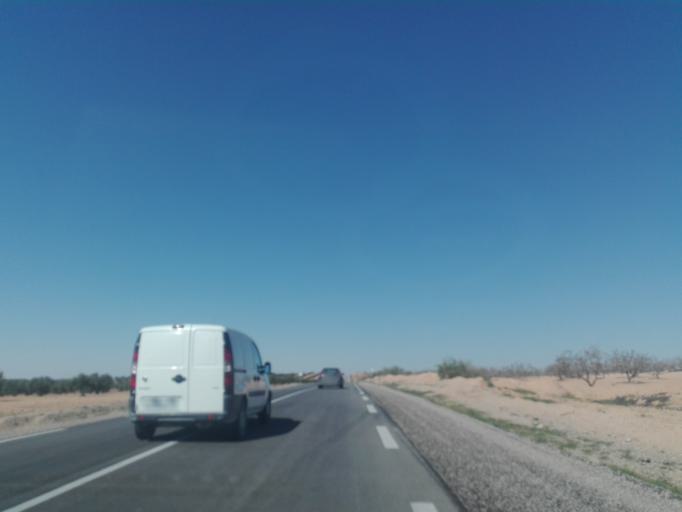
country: TN
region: Safaqis
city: Bi'r `Ali Bin Khalifah
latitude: 34.7583
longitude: 10.2897
